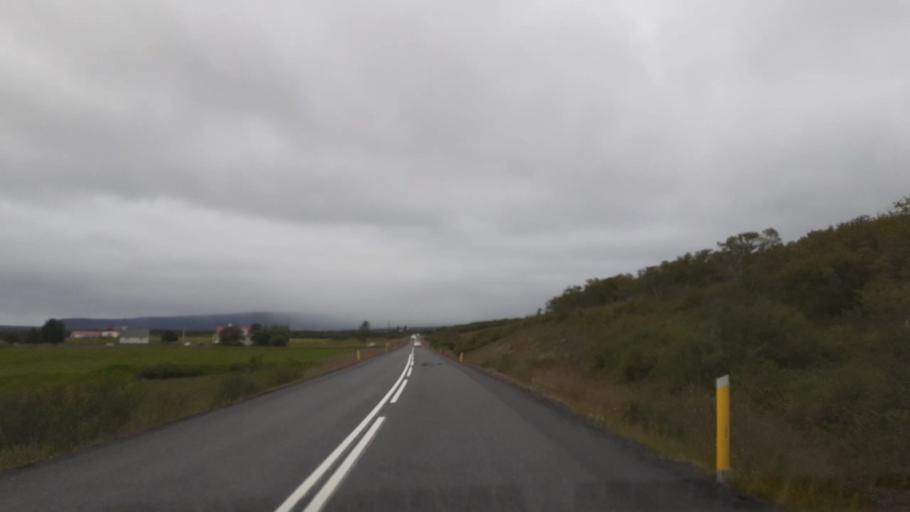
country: IS
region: Northeast
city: Husavik
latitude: 66.0653
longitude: -16.4424
